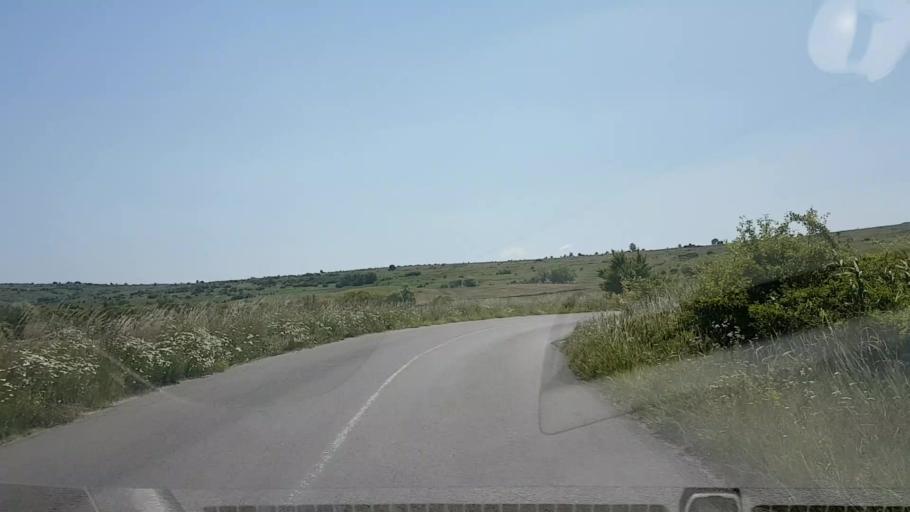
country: RO
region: Brasov
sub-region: Comuna Cincu
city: Cincu
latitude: 45.9542
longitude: 24.7819
